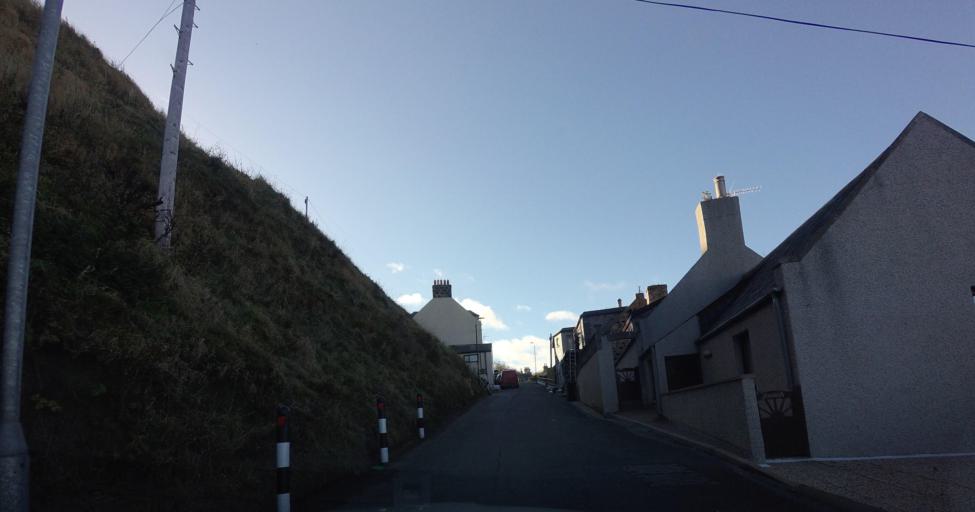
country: GB
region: Scotland
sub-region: Aberdeenshire
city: Macduff
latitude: 57.6729
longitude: -2.3363
